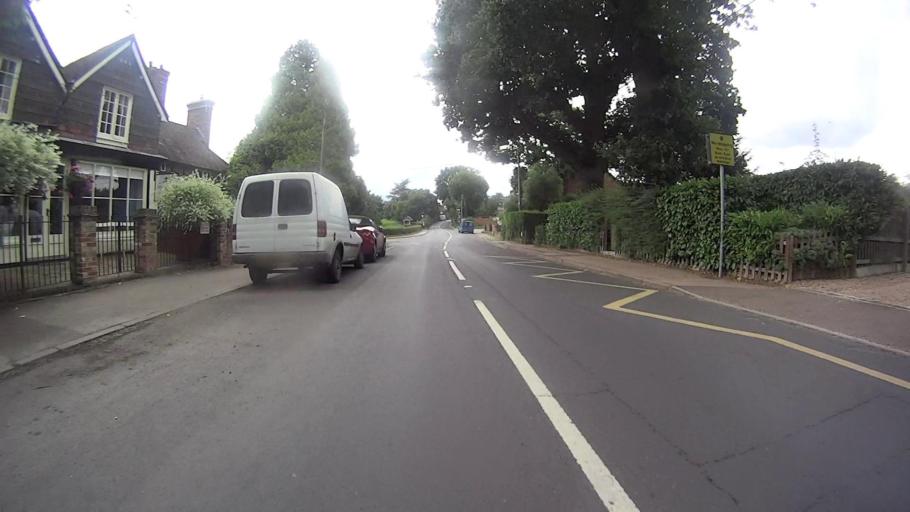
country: GB
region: England
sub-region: Surrey
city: Newdigate
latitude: 51.1662
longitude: -0.2895
